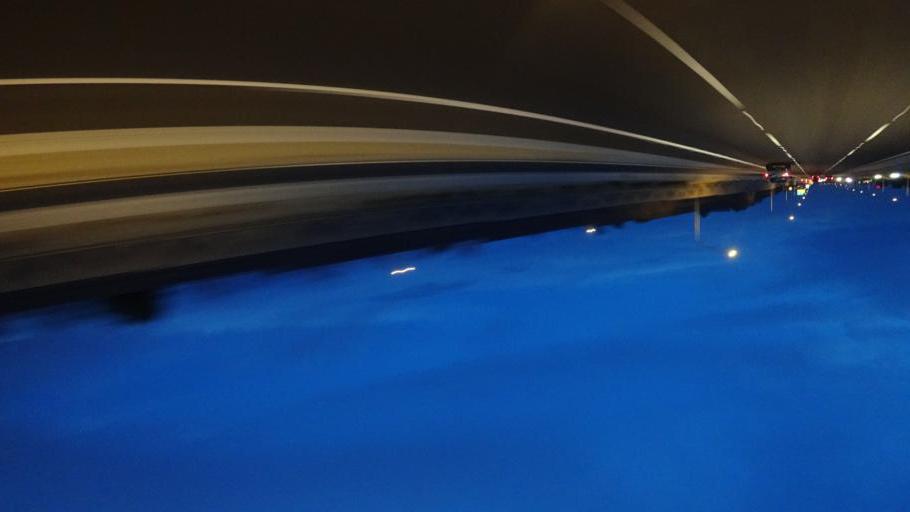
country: US
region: Arizona
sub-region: Maricopa County
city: Citrus Park
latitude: 33.6276
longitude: -112.4179
